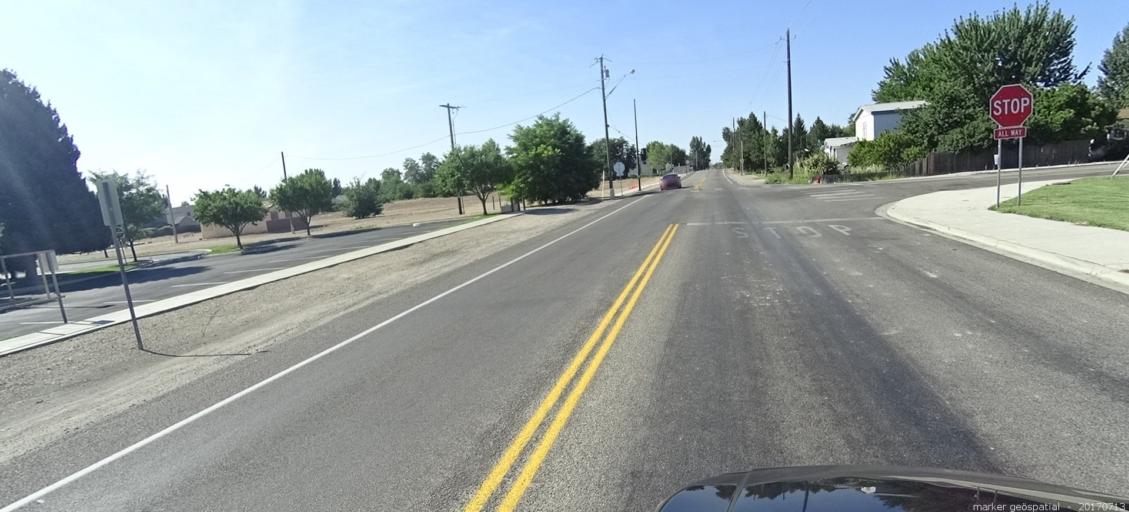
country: US
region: Idaho
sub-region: Ada County
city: Kuna
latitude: 43.4962
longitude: -116.4137
